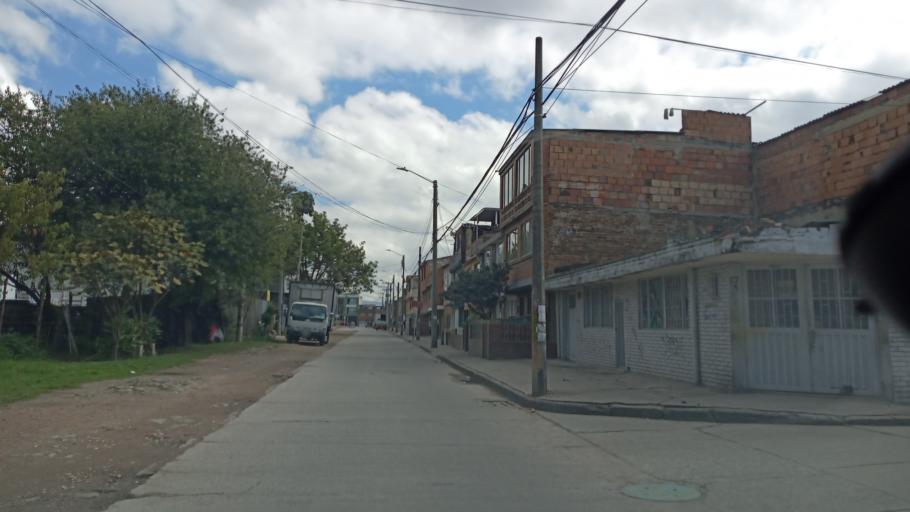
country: CO
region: Bogota D.C.
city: Bogota
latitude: 4.6825
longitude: -74.1286
